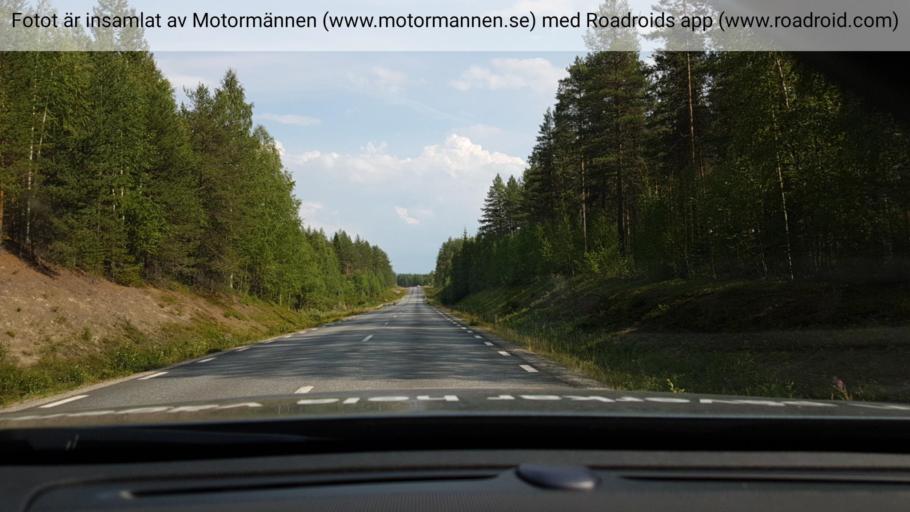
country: SE
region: Vaesterbotten
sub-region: Lycksele Kommun
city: Lycksele
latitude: 64.3896
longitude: 19.0913
